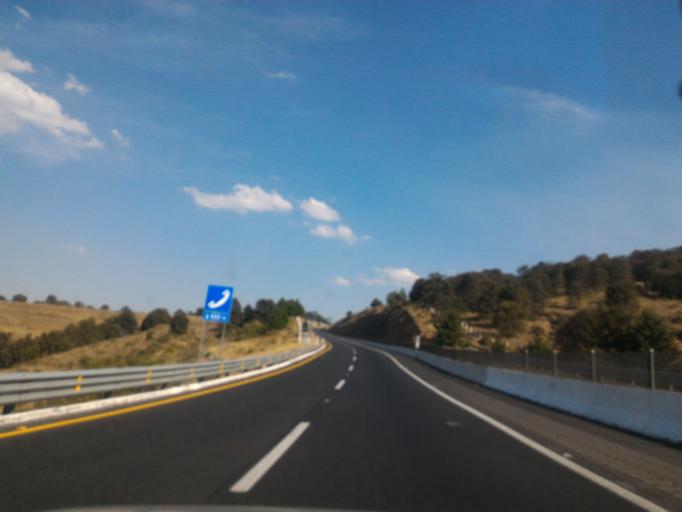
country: MX
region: Mexico
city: Temascalcingo de Jose Maria Velazco
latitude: 19.8531
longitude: -100.0146
